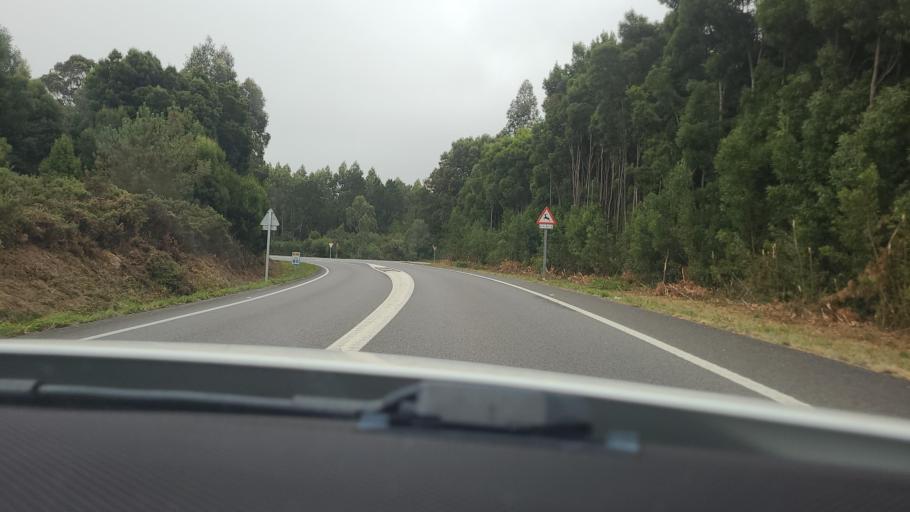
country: ES
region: Galicia
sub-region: Provincia da Coruna
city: Dumbria
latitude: 43.0206
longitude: -9.1154
